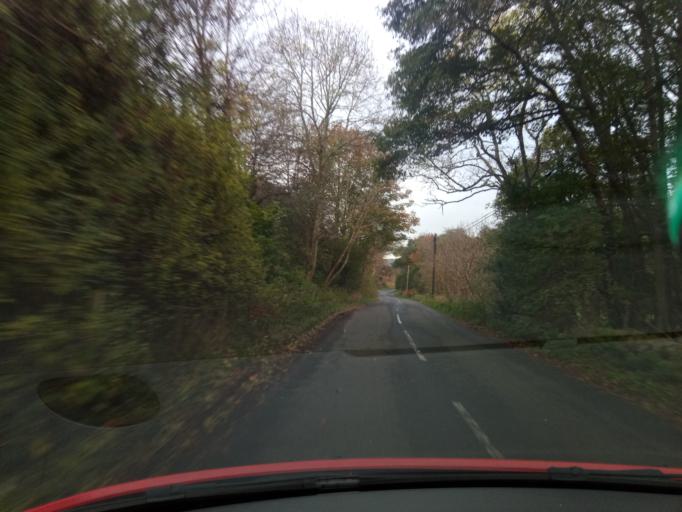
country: GB
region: Scotland
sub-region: The Scottish Borders
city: Galashiels
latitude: 55.6139
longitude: -2.8764
